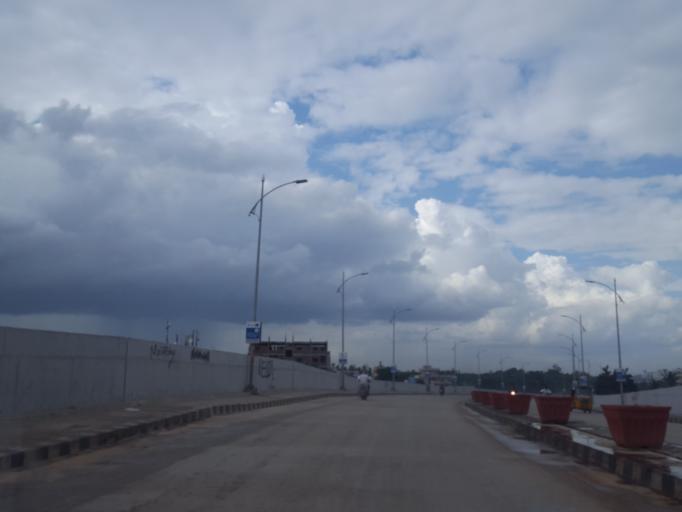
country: IN
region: Telangana
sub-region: Medak
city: Serilingampalle
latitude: 17.4816
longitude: 78.3110
